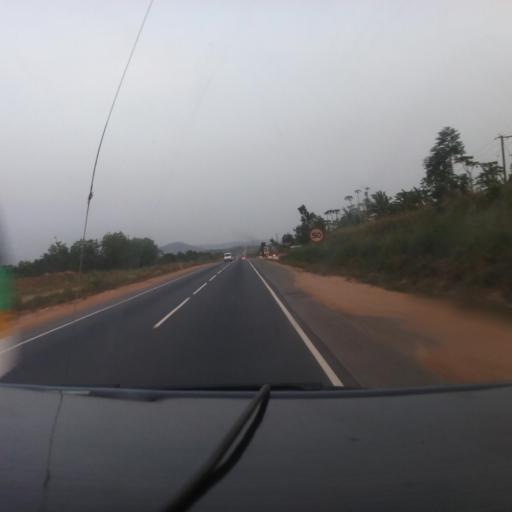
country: GH
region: Eastern
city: Nsawam
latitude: 5.8765
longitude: -0.3717
